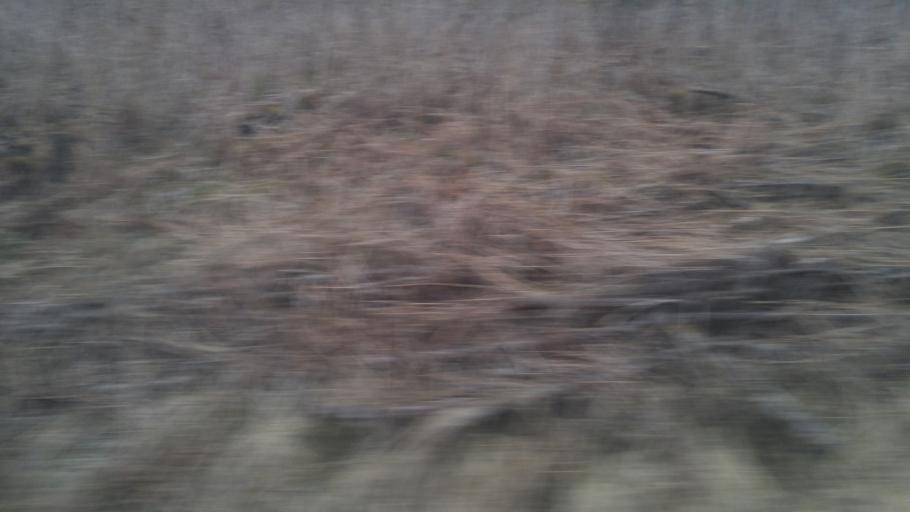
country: NO
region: Akershus
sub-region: Eidsvoll
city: Eidsvoll
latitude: 60.3696
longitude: 11.2430
